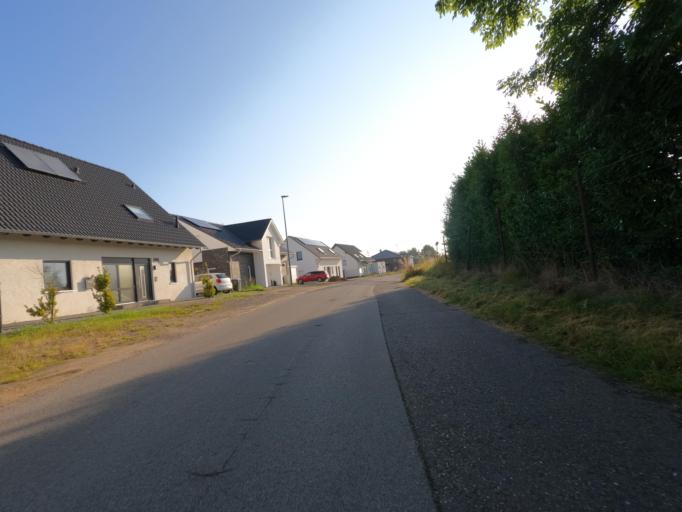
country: DE
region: North Rhine-Westphalia
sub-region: Regierungsbezirk Koln
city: Titz
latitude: 51.0080
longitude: 6.4319
